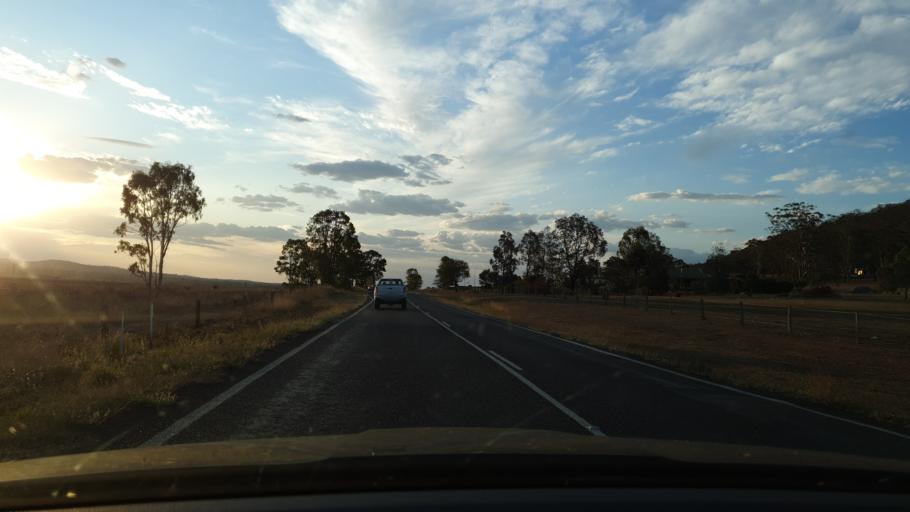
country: AU
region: Queensland
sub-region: Southern Downs
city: Warwick
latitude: -28.1844
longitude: 151.9970
